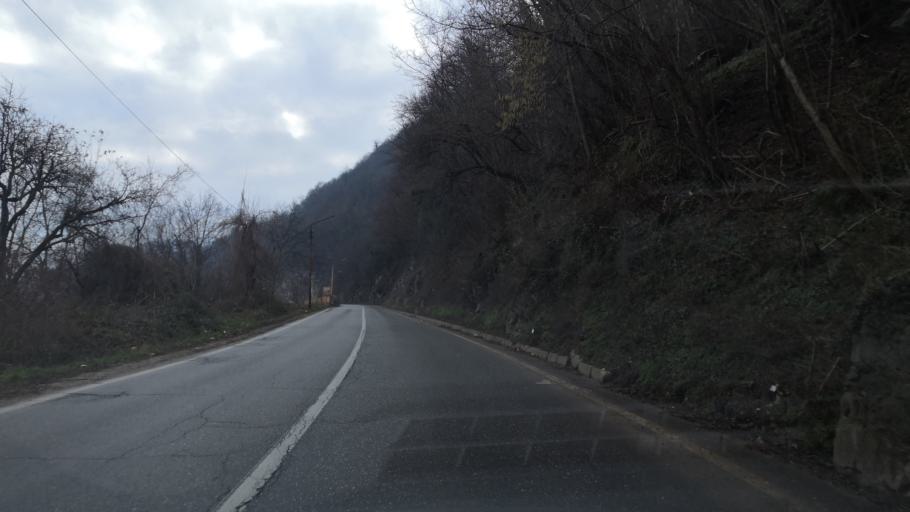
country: RS
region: Central Serbia
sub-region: Macvanski Okrug
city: Mali Zvornik
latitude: 44.3682
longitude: 19.1031
